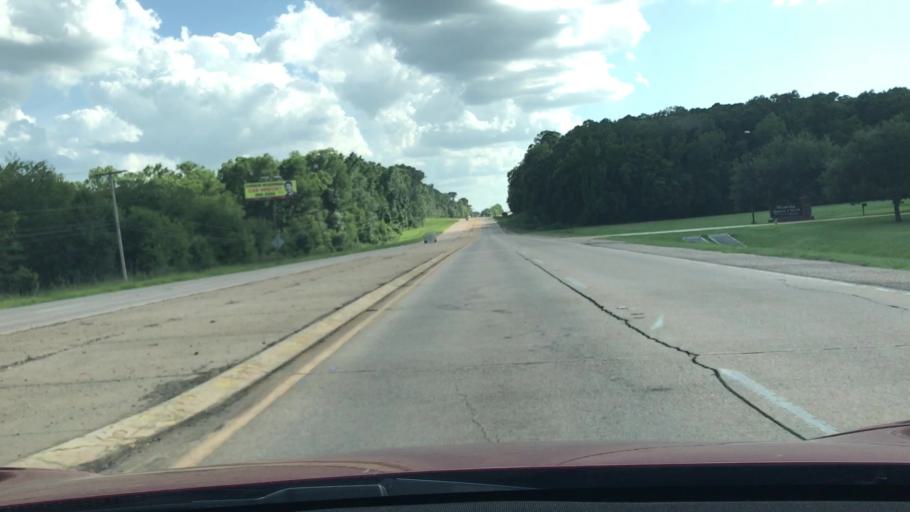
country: US
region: Louisiana
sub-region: Bossier Parish
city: Bossier City
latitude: 32.4081
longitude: -93.7271
